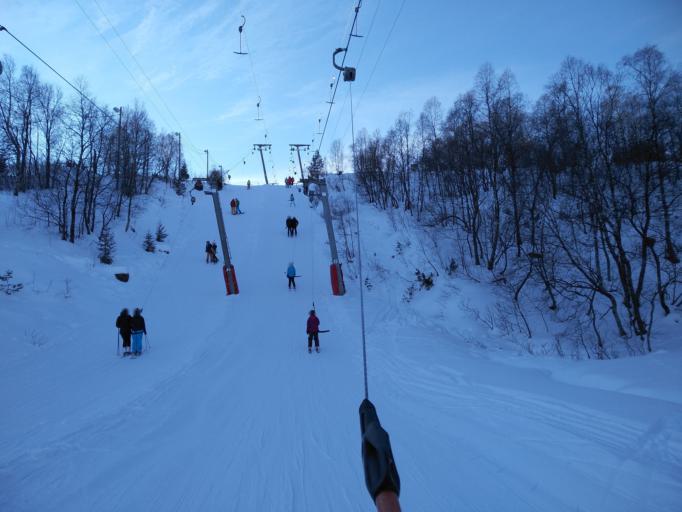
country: NO
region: Rogaland
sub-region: Sauda
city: Sauda
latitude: 59.6222
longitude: 6.2402
